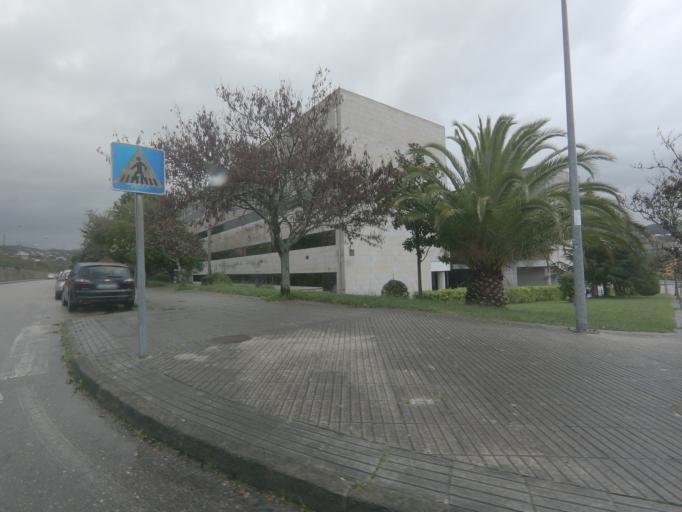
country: ES
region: Galicia
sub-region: Provincia de Pontevedra
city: Pontevedra
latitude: 42.4399
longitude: -8.6388
